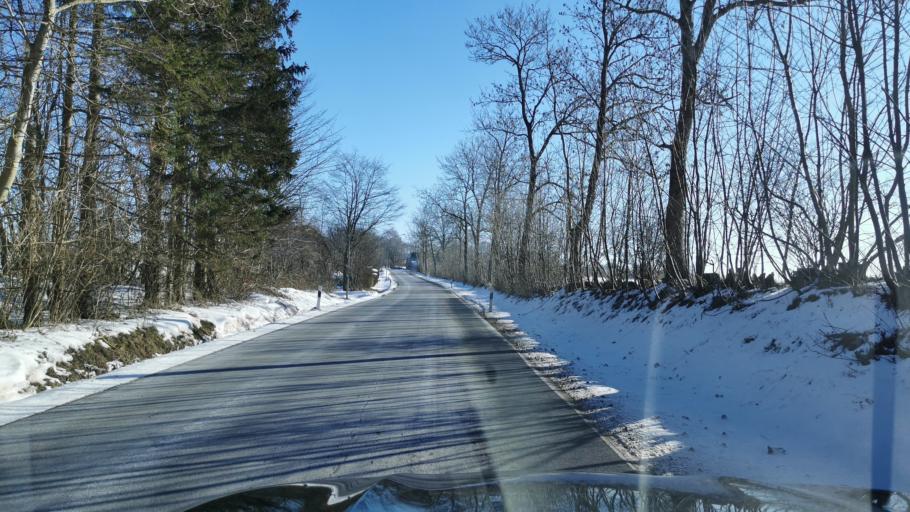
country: DE
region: Schleswig-Holstein
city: Sorup
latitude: 54.7323
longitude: 9.6490
